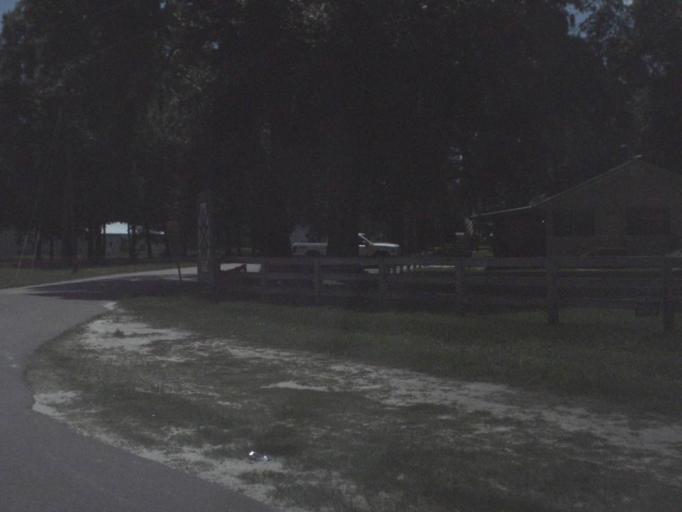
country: US
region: Florida
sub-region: Gilchrist County
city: Trenton
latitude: 29.6209
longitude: -82.8156
